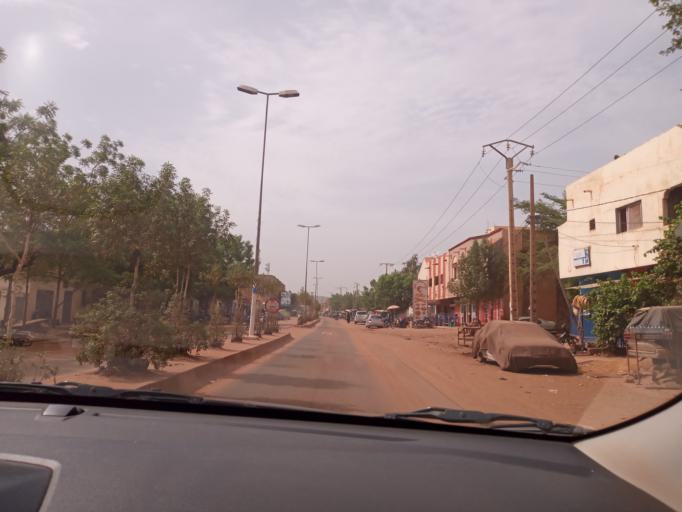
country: ML
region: Bamako
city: Bamako
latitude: 12.6727
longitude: -7.9241
